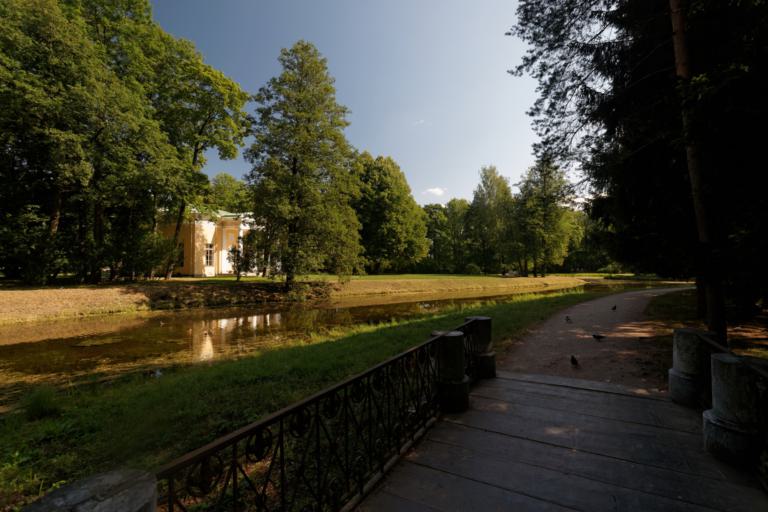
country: RU
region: St.-Petersburg
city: Pushkin
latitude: 59.7130
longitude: 30.3875
